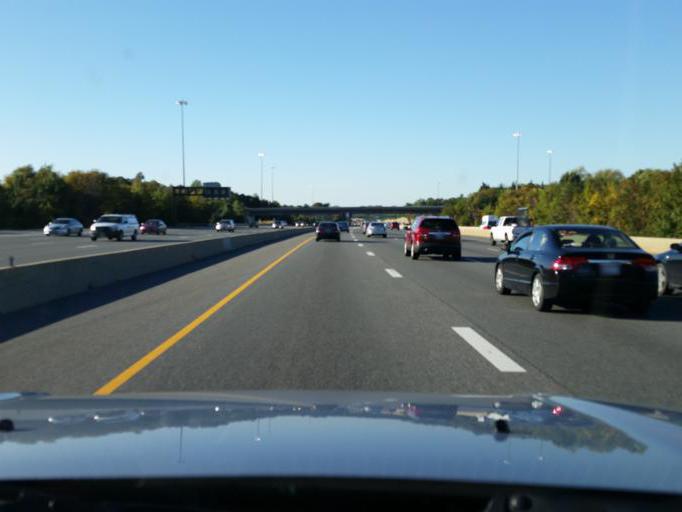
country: US
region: Maryland
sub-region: Montgomery County
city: Gaithersburg
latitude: 39.1198
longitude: -77.1969
